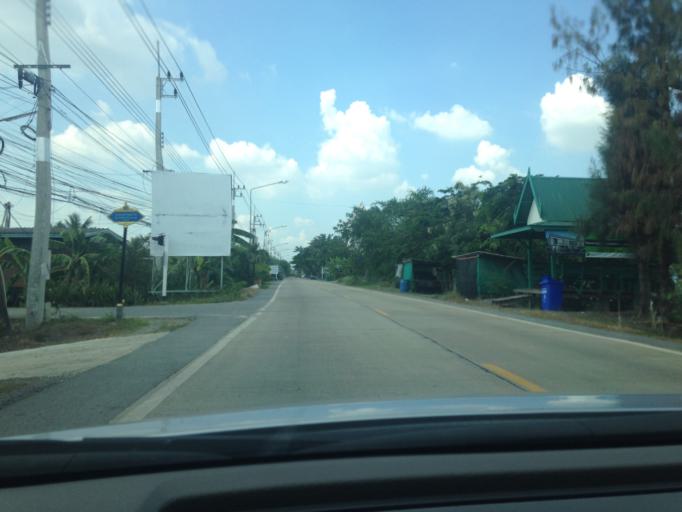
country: TH
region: Phra Nakhon Si Ayutthaya
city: Ban Bang Kadi Pathum Thani
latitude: 14.0334
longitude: 100.5930
